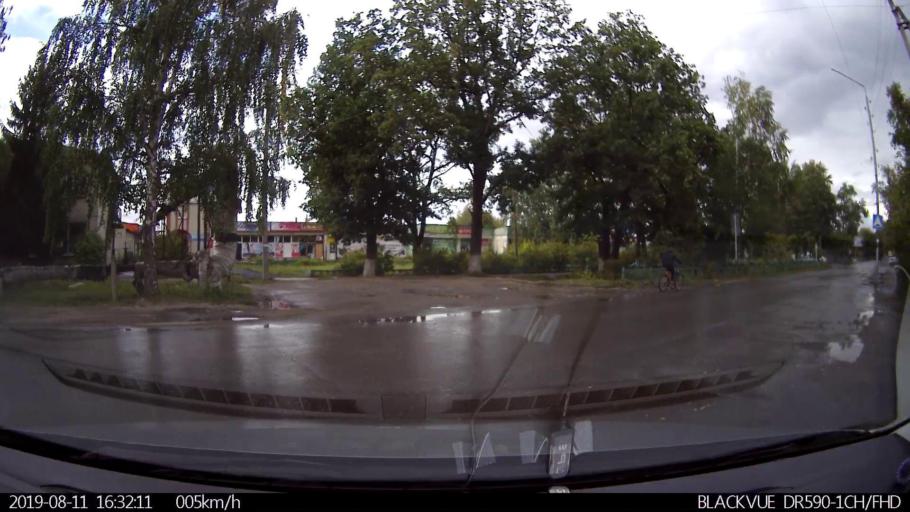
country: RU
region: Ulyanovsk
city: Mayna
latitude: 54.1115
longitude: 47.6201
